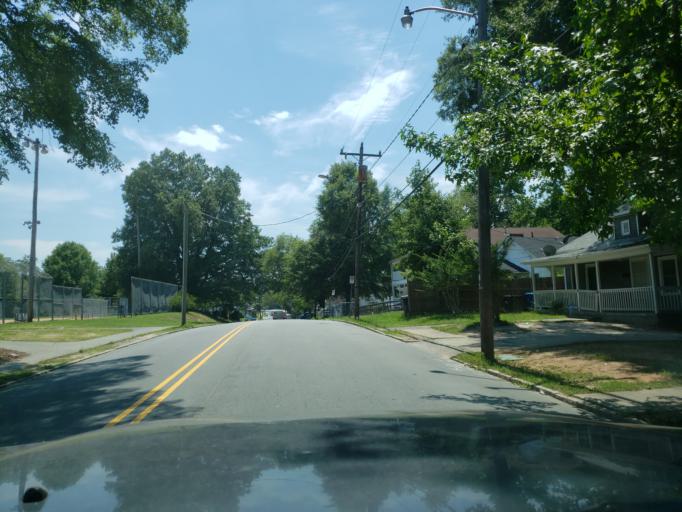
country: US
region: North Carolina
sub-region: Durham County
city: Durham
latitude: 35.9819
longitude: -78.9038
